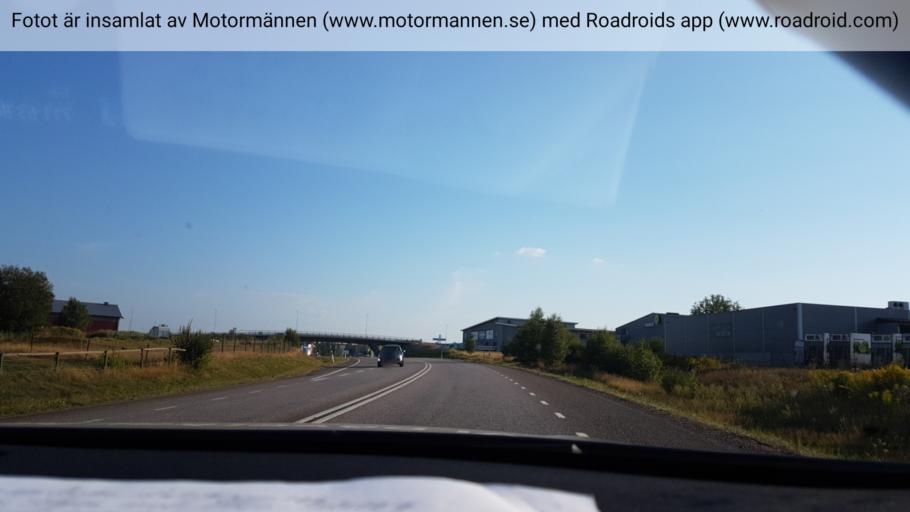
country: SE
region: Vaestra Goetaland
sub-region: Skovde Kommun
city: Skoevde
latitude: 58.4154
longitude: 13.8824
